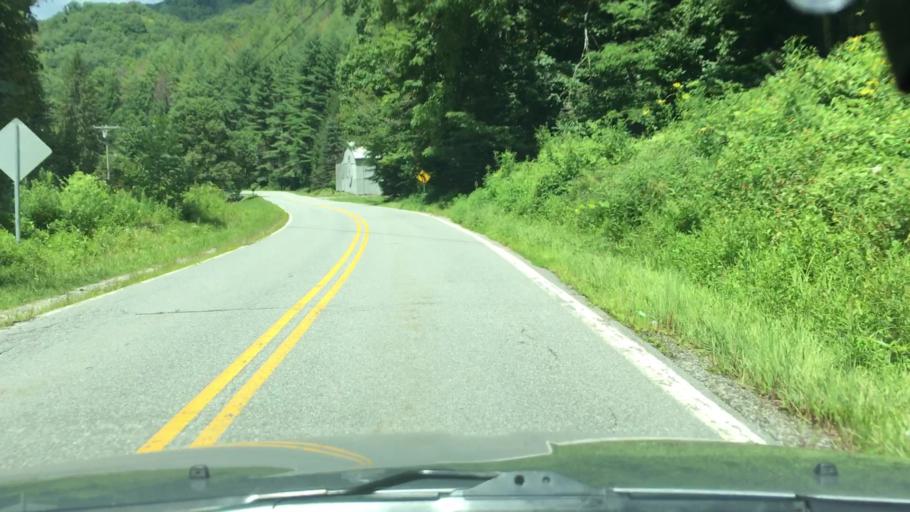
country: US
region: North Carolina
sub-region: Madison County
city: Mars Hill
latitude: 35.9187
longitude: -82.5373
